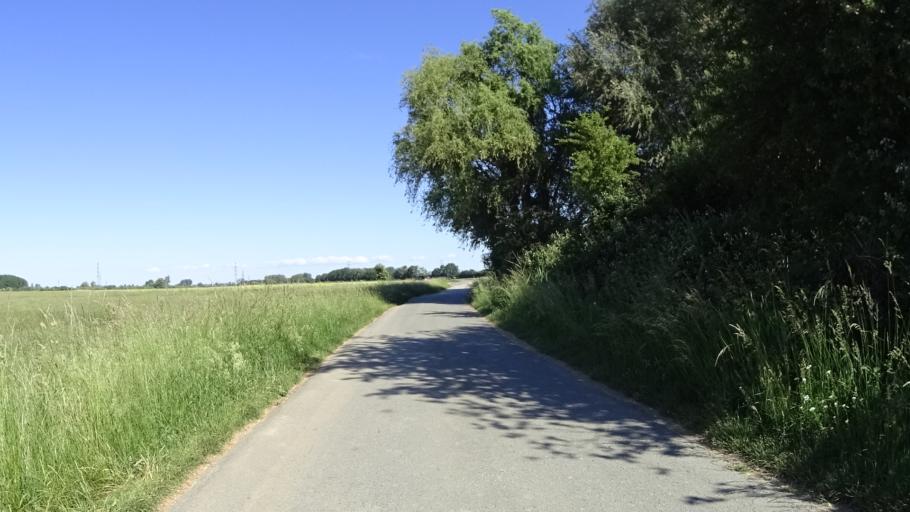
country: DE
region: Hesse
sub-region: Regierungsbezirk Darmstadt
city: Alsbach-Hahnlein
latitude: 49.7541
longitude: 8.5845
